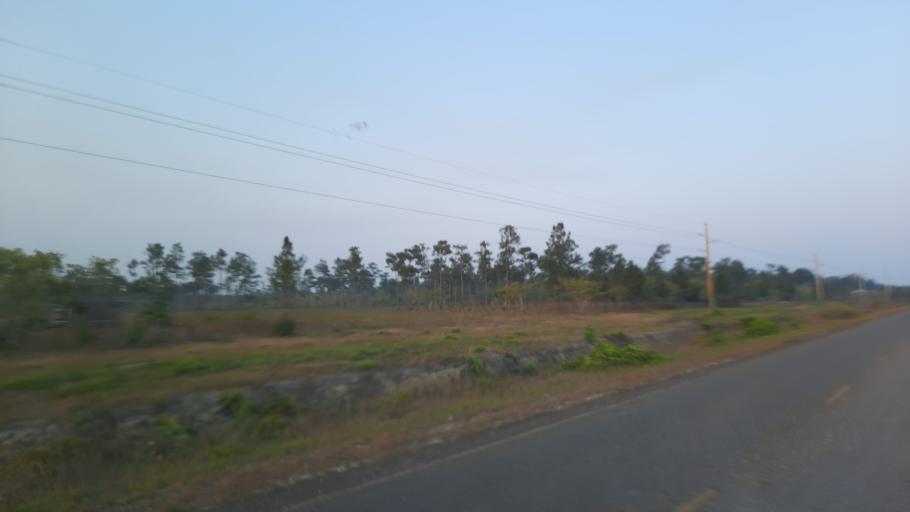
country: BZ
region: Stann Creek
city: Placencia
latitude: 16.5315
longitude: -88.4594
